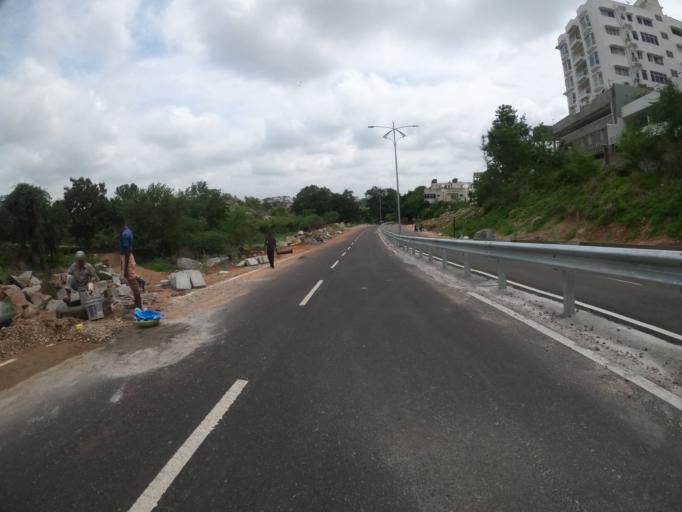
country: IN
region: Telangana
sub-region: Rangareddi
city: Kukatpalli
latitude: 17.4215
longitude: 78.3980
